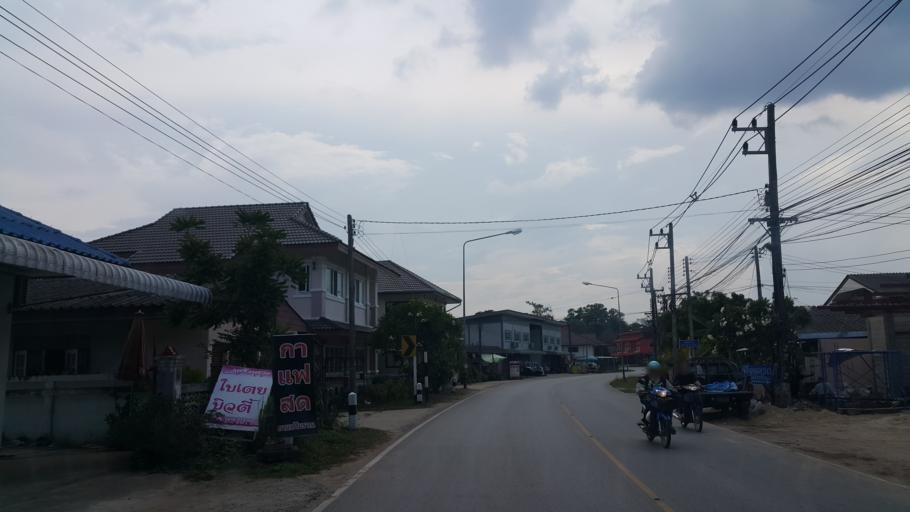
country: TH
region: Chiang Rai
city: Chiang Rai
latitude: 19.9124
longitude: 99.8842
